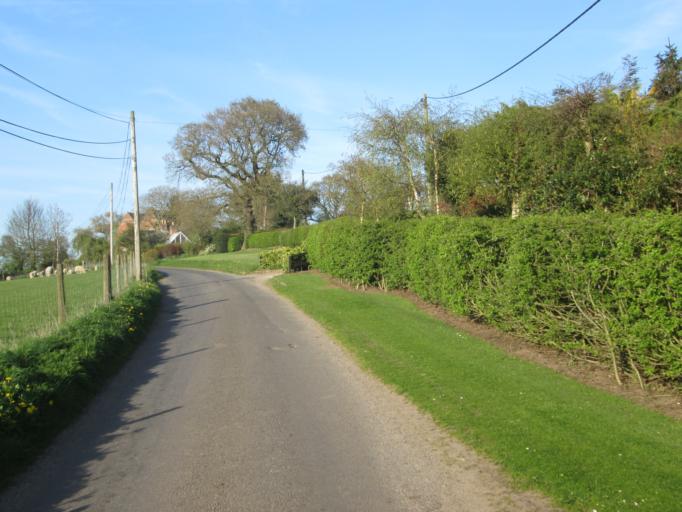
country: GB
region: England
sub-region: Derbyshire
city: Shirley
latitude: 52.9509
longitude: -1.6335
